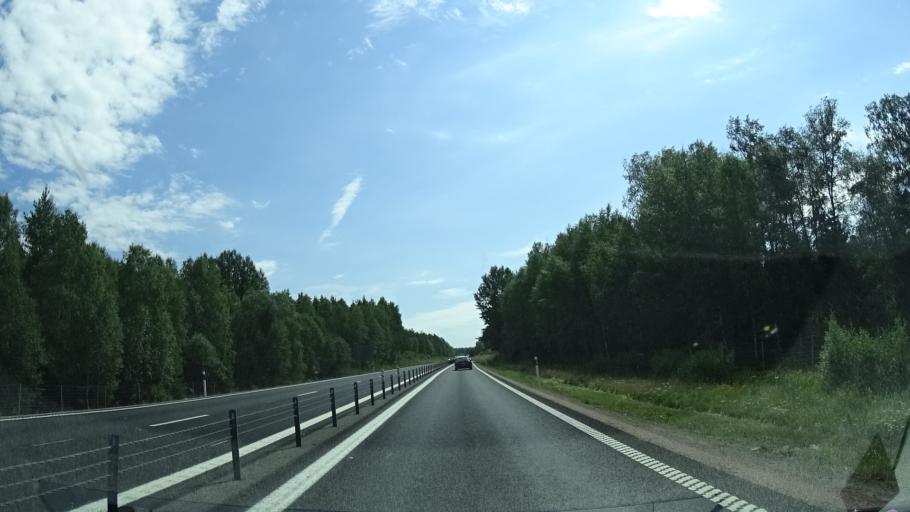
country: SE
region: Vaermland
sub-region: Karlstads Kommun
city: Skattkarr
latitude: 59.3870
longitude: 13.8675
